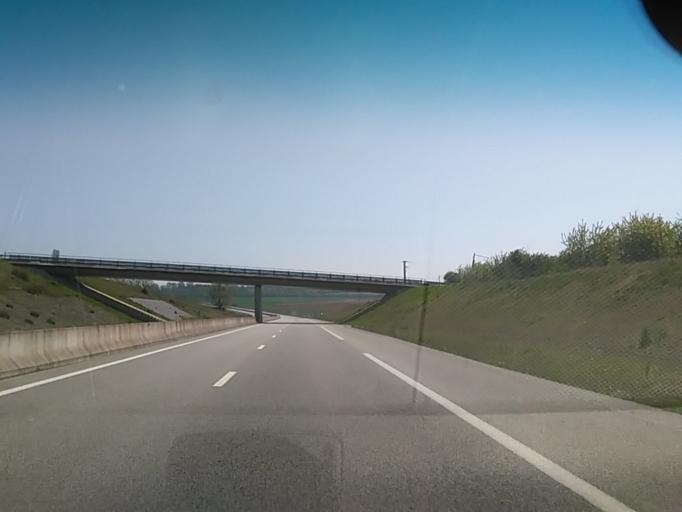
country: FR
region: Lower Normandy
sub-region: Departement de l'Orne
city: Sees
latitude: 48.6448
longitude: 0.1371
